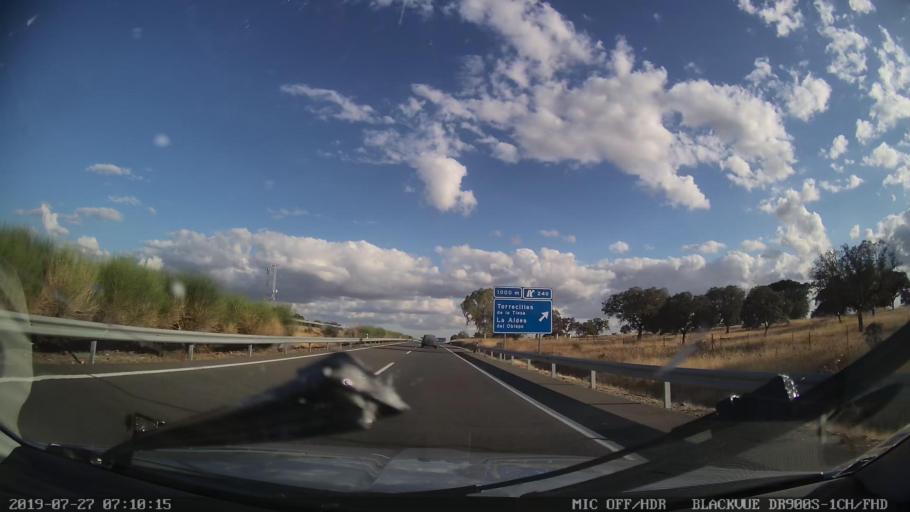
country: ES
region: Extremadura
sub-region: Provincia de Caceres
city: Jaraicejo
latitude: 39.5784
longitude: -5.8347
